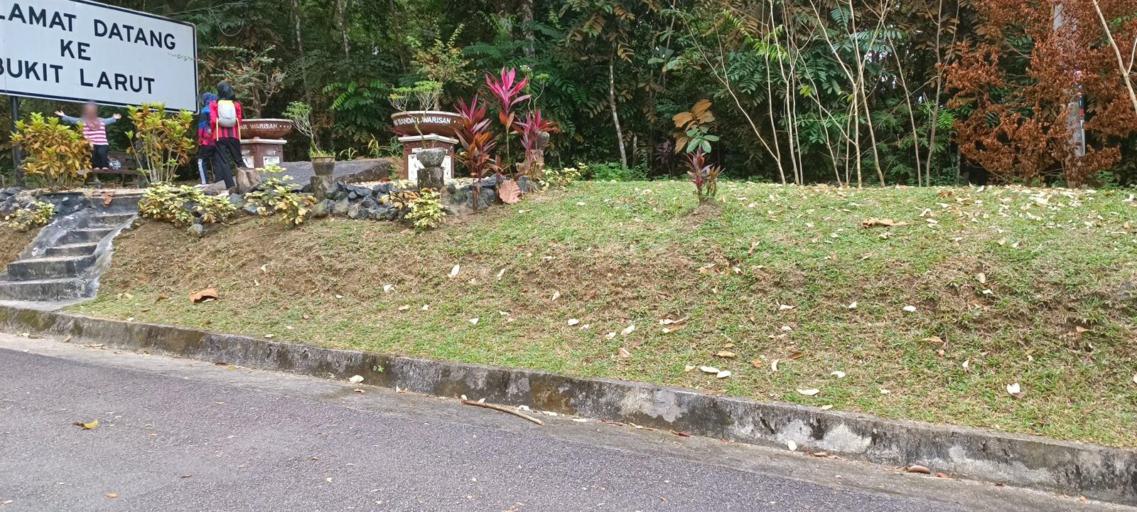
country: MY
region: Perak
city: Taiping
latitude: 4.8603
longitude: 100.7608
